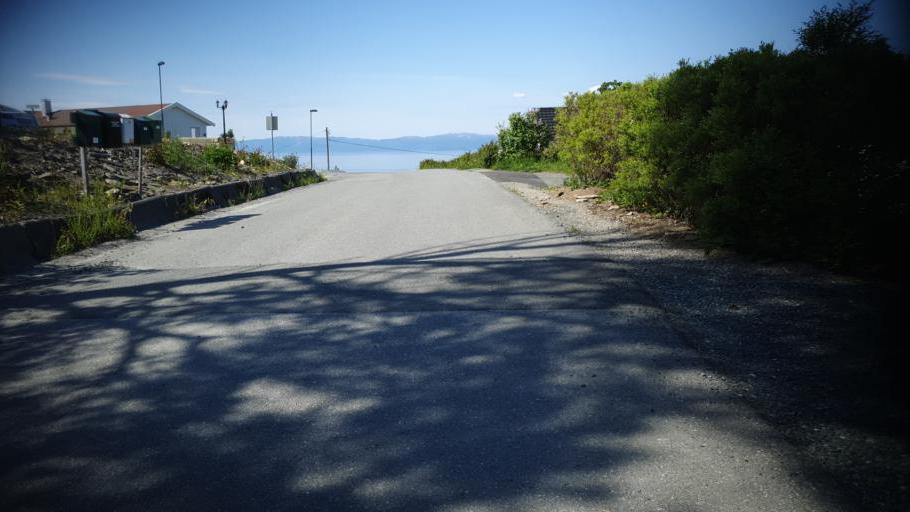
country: NO
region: Sor-Trondelag
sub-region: Malvik
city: Malvik
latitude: 63.4380
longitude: 10.6463
